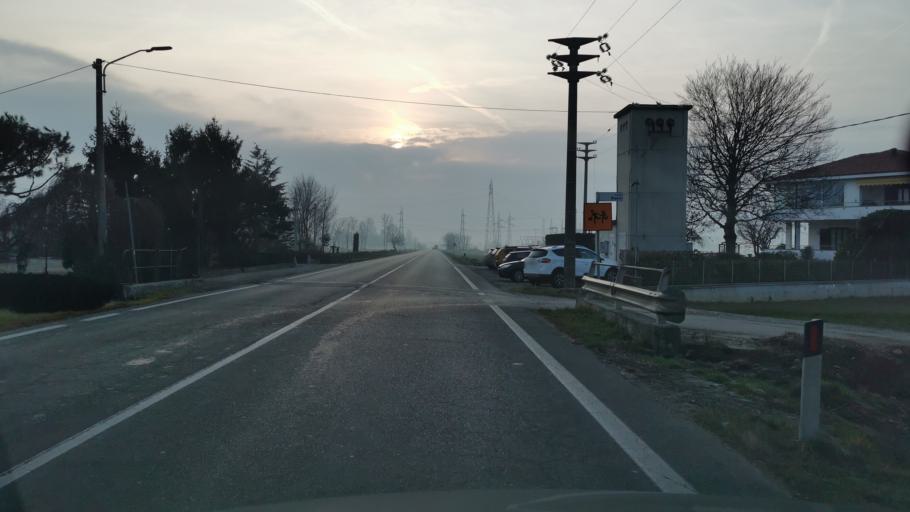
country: IT
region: Piedmont
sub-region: Provincia di Torino
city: Ciconio
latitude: 45.3427
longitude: 7.7693
